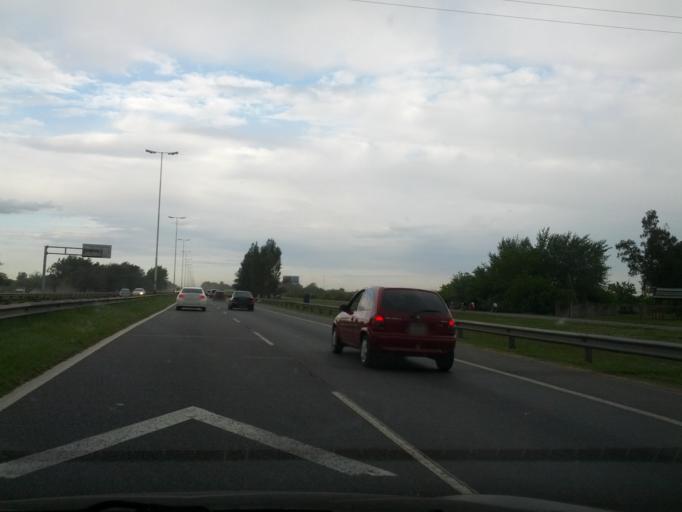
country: AR
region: Buenos Aires
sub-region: Partido de General Rodriguez
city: General Rodriguez
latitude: -34.5837
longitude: -58.9913
